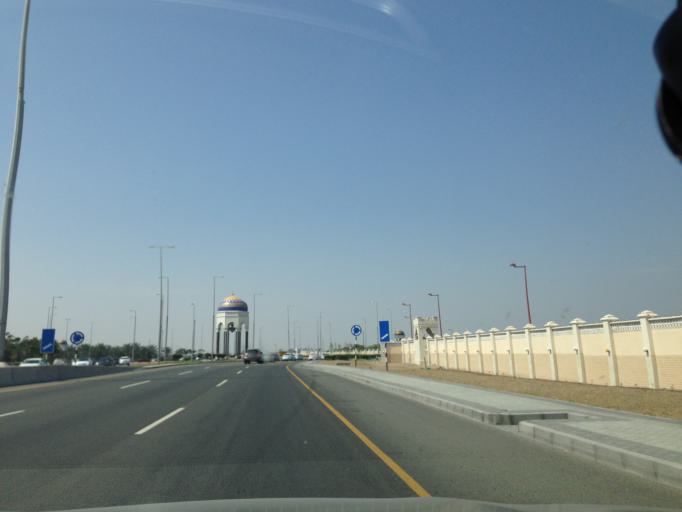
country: OM
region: Muhafazat Masqat
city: As Sib al Jadidah
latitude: 23.6626
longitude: 58.1729
